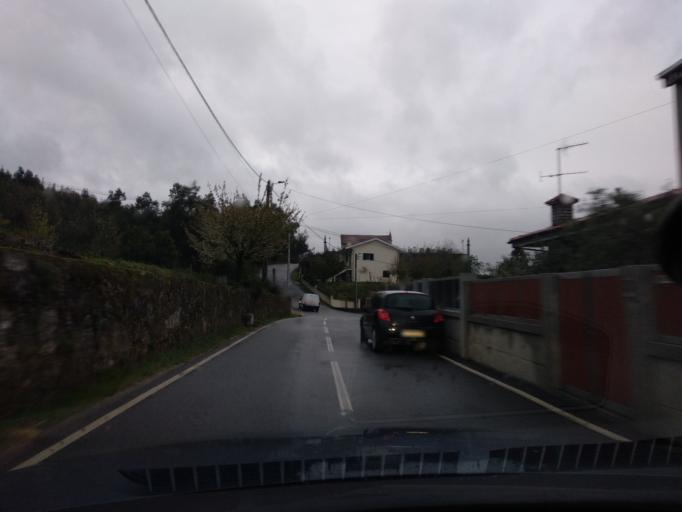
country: PT
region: Porto
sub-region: Penafiel
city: Penafiel
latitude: 41.1868
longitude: -8.2900
